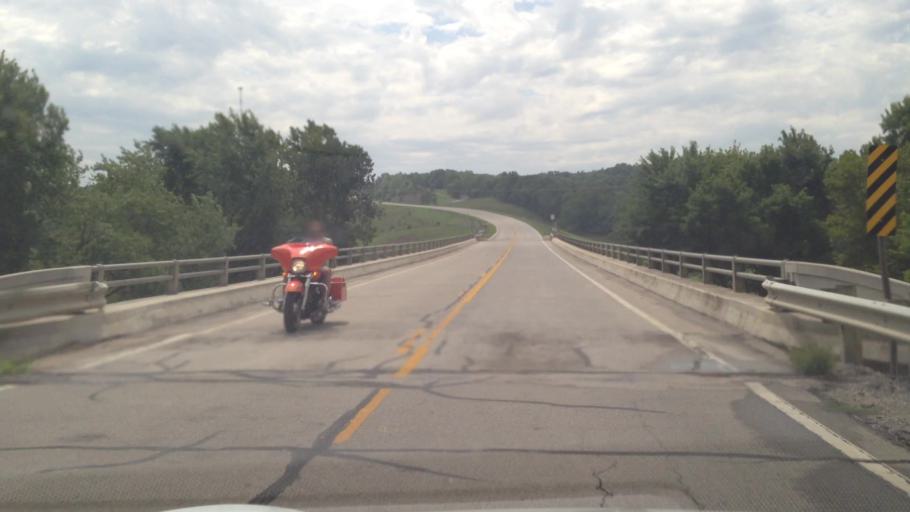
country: US
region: Kansas
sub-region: Bourbon County
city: Fort Scott
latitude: 37.8359
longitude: -94.9813
